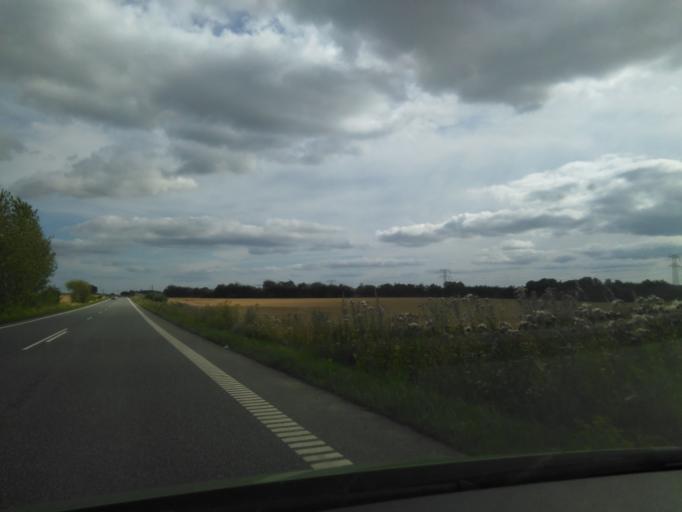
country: DK
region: Central Jutland
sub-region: Arhus Kommune
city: Kolt
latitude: 56.1050
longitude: 10.0580
